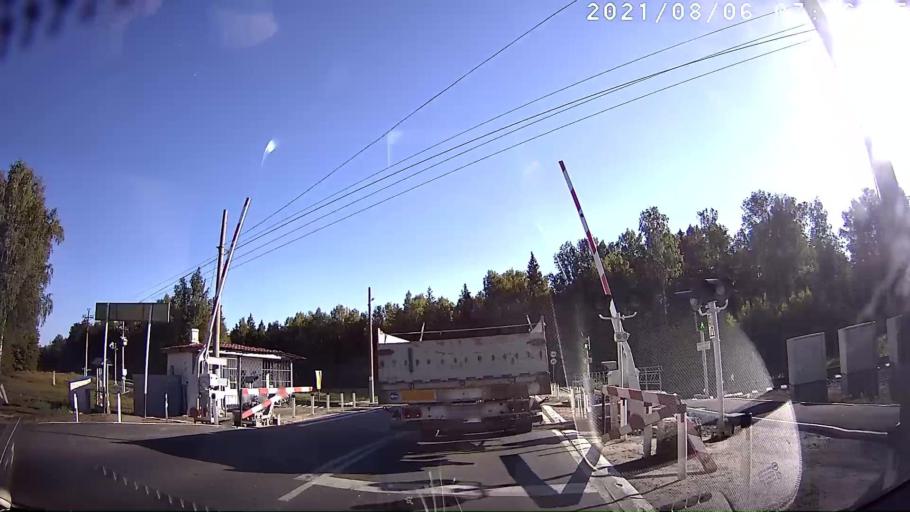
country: RU
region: Mariy-El
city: Yoshkar-Ola
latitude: 56.5604
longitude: 47.9803
